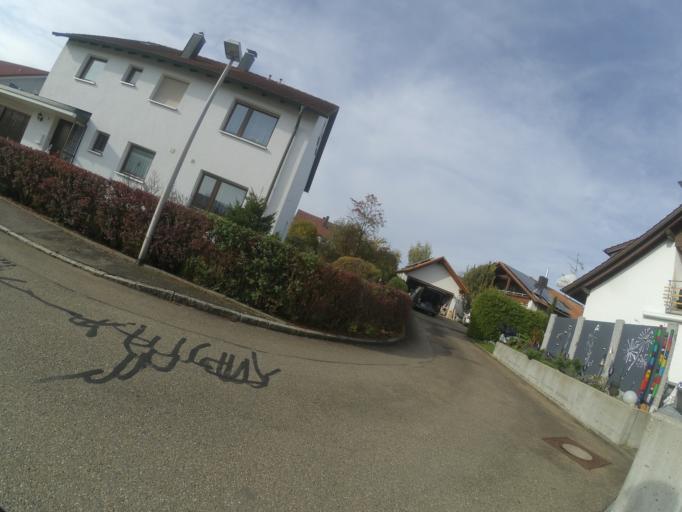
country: DE
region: Baden-Wuerttemberg
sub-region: Tuebingen Region
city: Blaubeuren
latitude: 48.4290
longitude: 9.8615
